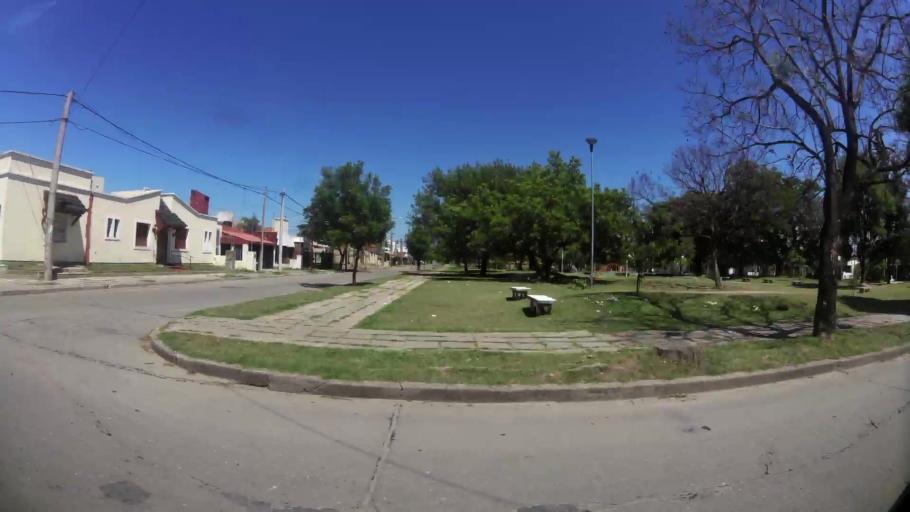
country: AR
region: Cordoba
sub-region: Departamento de Capital
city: Cordoba
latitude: -31.4251
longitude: -64.2097
